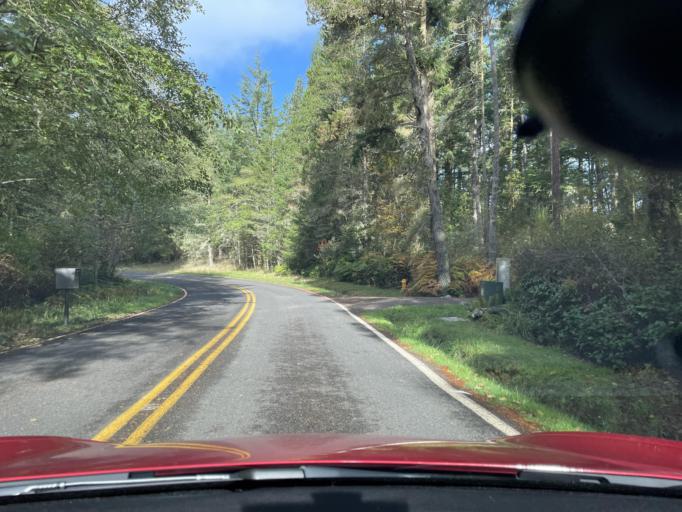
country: US
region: Washington
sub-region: San Juan County
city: Friday Harbor
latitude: 48.5251
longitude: -122.9741
